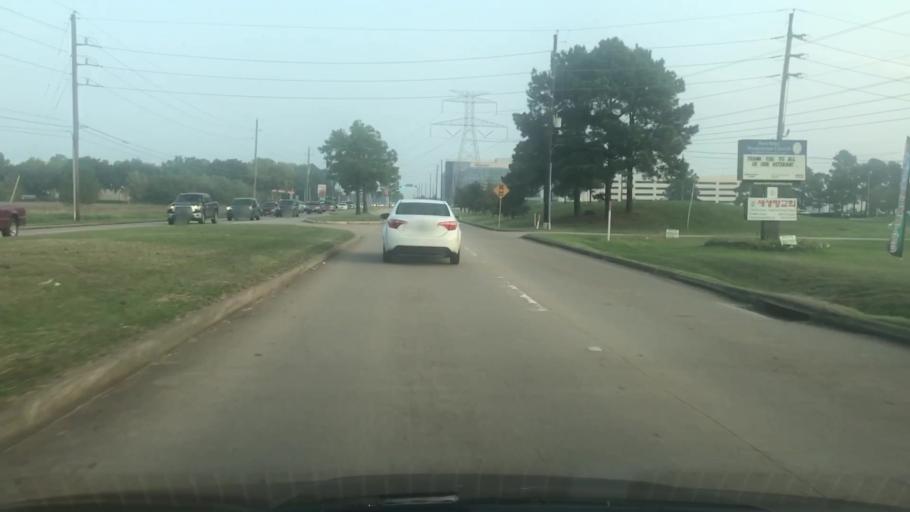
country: US
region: Texas
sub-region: Fort Bend County
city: Cinco Ranch
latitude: 29.7917
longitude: -95.7518
